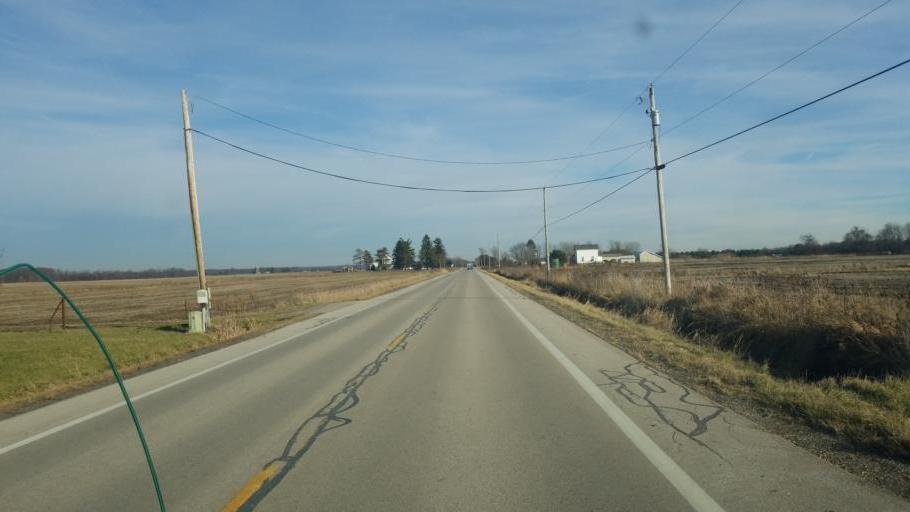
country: US
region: Ohio
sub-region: Ashtabula County
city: Andover
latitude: 41.5353
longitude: -80.6911
